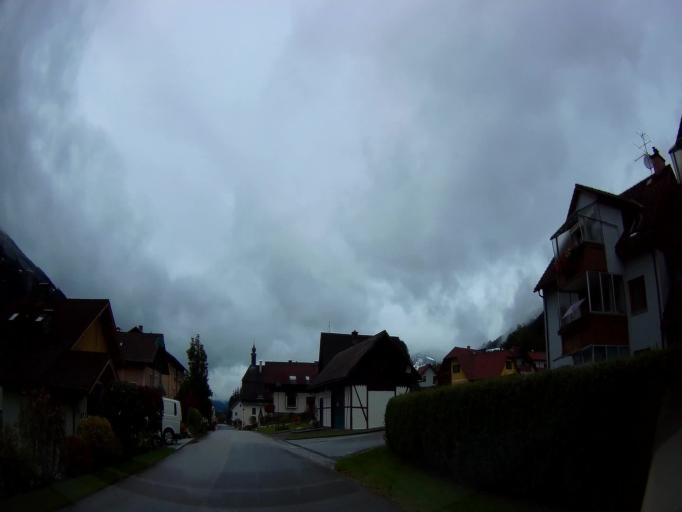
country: AT
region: Styria
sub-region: Politischer Bezirk Liezen
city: Treglwang
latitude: 47.4752
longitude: 14.5930
